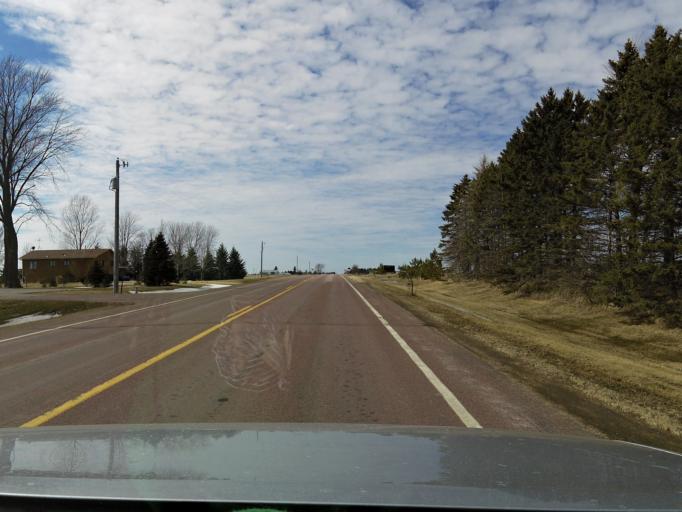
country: US
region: Minnesota
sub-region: Le Sueur County
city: Montgomery
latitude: 44.4859
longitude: -93.6723
